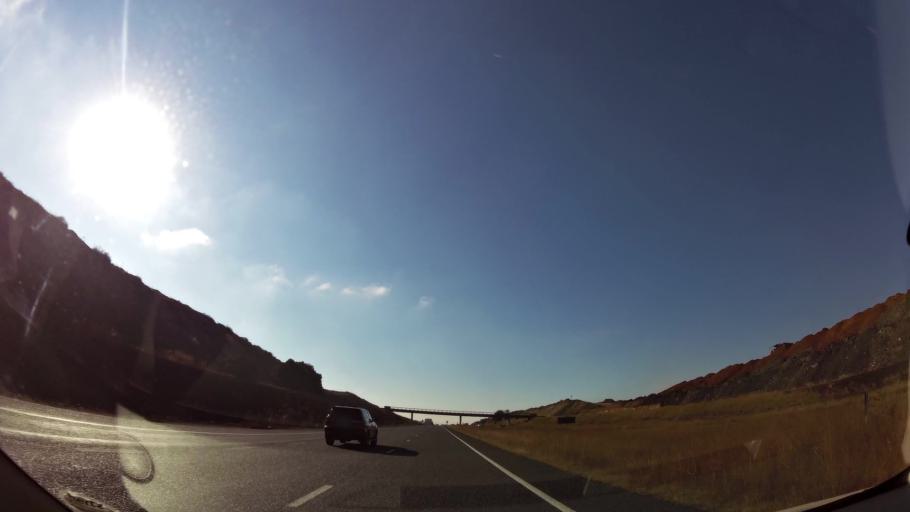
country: ZA
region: Mpumalanga
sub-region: Nkangala District Municipality
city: Witbank
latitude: -26.0175
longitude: 28.9677
